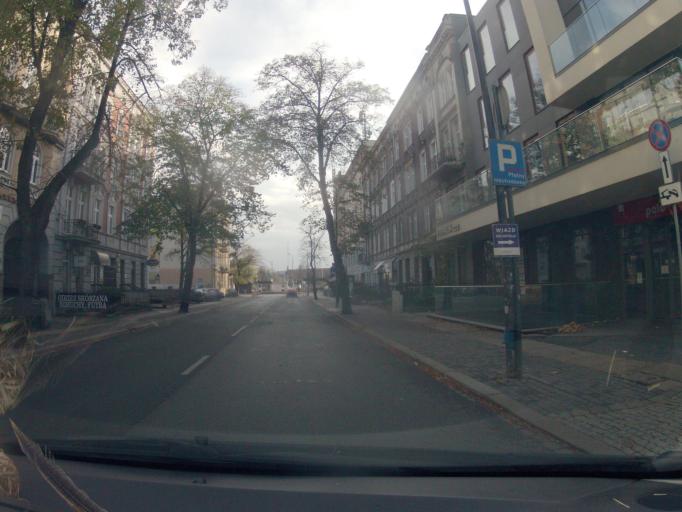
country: PL
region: Opole Voivodeship
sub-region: Powiat opolski
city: Opole
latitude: 50.6642
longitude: 17.9275
